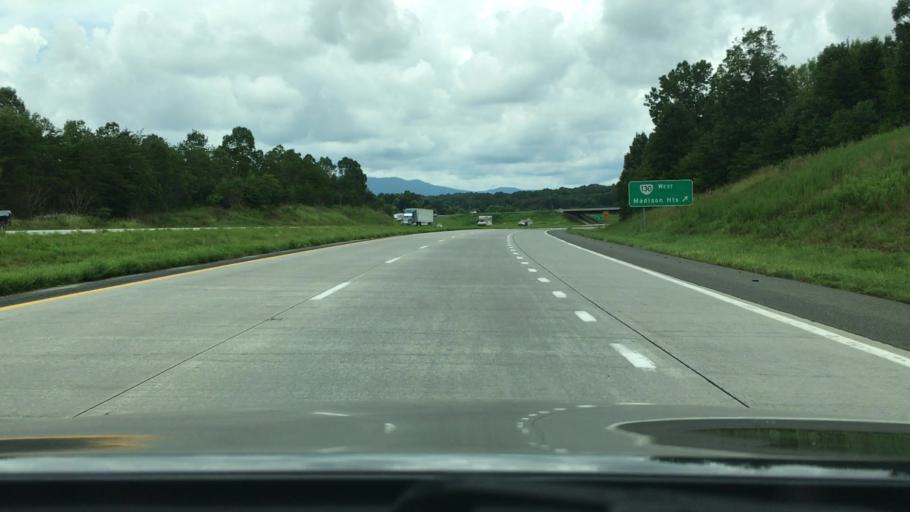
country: US
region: Virginia
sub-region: Amherst County
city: Madison Heights
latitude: 37.4590
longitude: -79.0813
